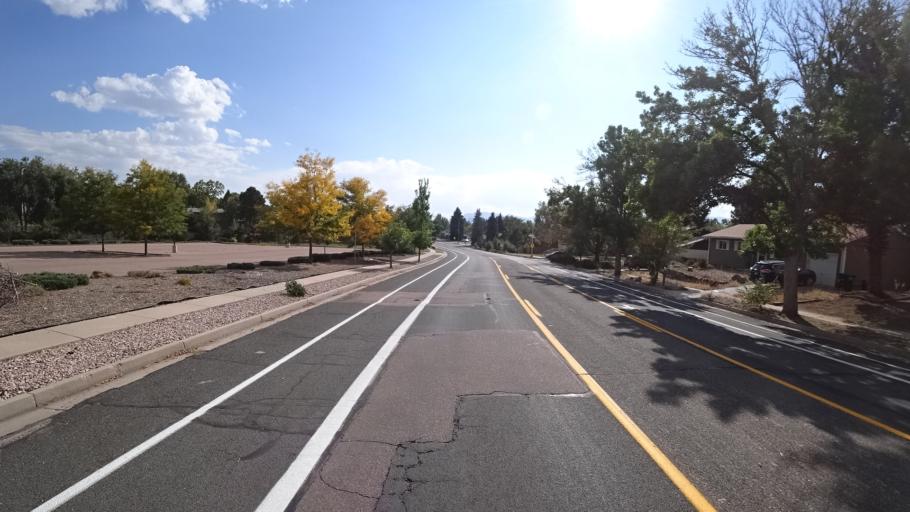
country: US
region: Colorado
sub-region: El Paso County
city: Cimarron Hills
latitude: 38.8807
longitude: -104.7392
